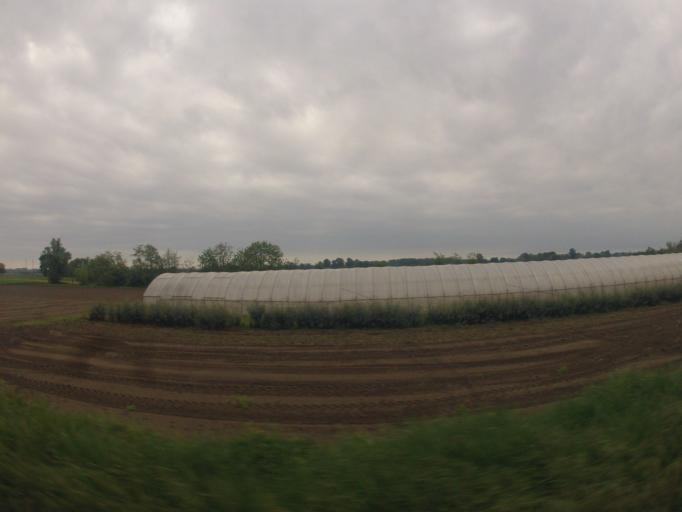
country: IT
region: Piedmont
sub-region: Provincia di Torino
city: Carignano
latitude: 44.8777
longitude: 7.6641
